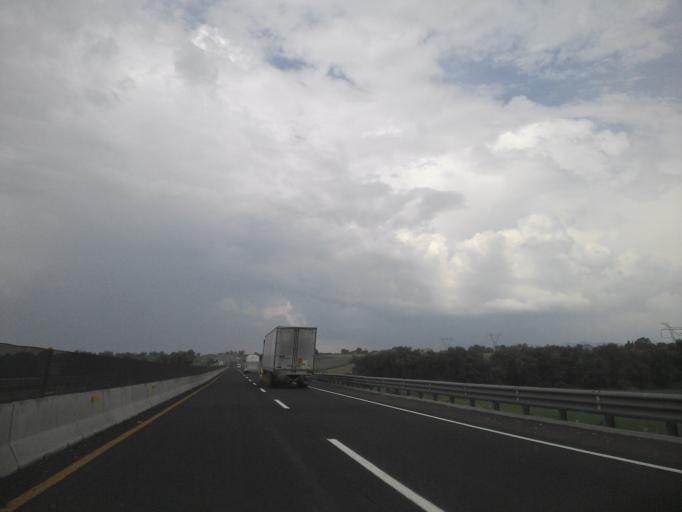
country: MX
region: Hidalgo
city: San Marcos
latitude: 20.0830
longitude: -99.3334
